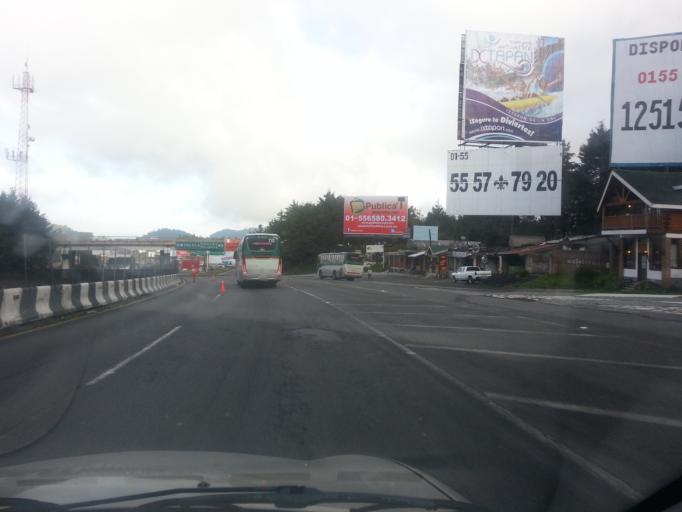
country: MX
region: Mexico
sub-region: Huixquilucan
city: El Palacio
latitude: 19.3019
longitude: -99.3688
